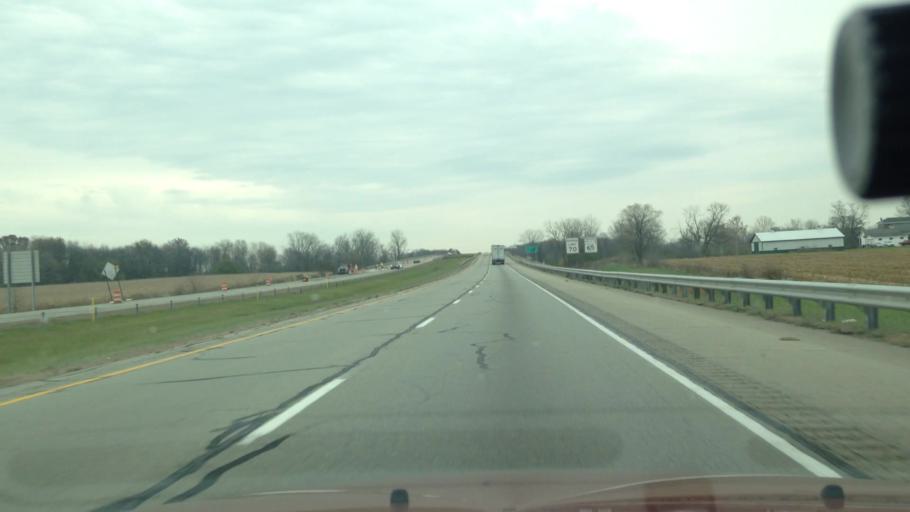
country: US
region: Indiana
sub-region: Wayne County
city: Cambridge City
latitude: 39.8521
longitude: -85.2524
